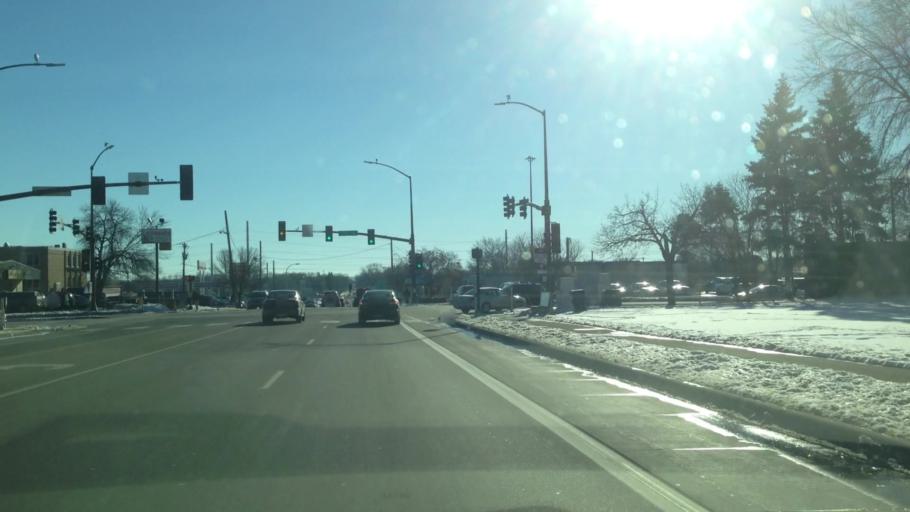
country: US
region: Minnesota
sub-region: Hennepin County
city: Richfield
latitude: 44.8644
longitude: -93.2682
